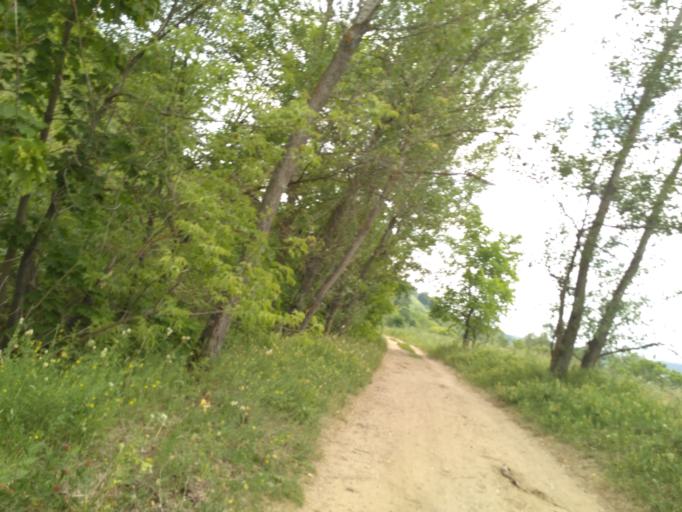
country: RU
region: Nizjnij Novgorod
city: Nizhniy Novgorod
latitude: 56.2744
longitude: 43.9713
